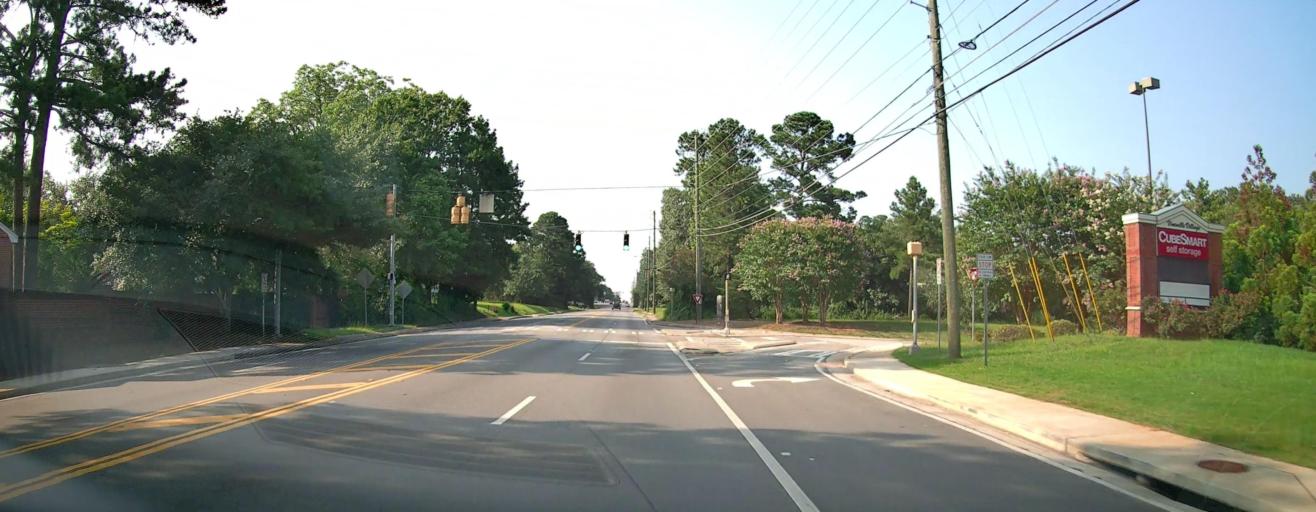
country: US
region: Georgia
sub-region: Bibb County
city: Macon
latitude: 32.8422
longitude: -83.6623
